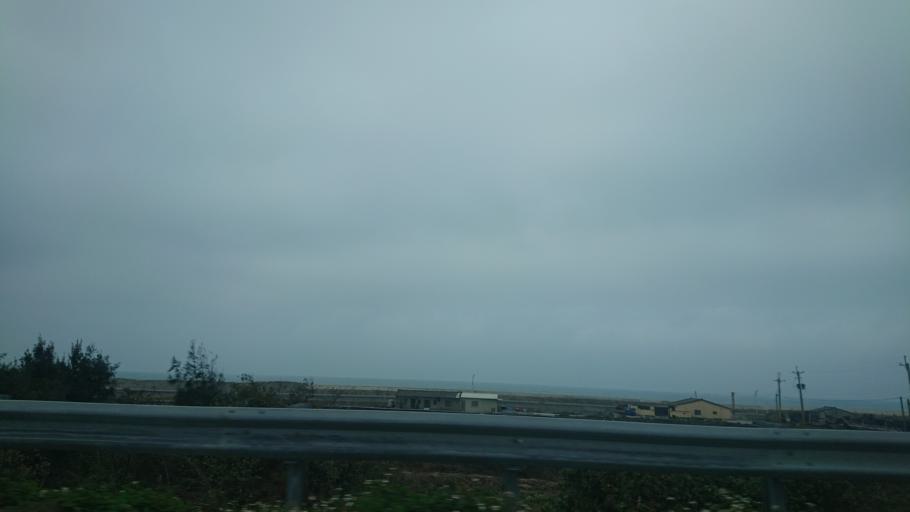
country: TW
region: Taiwan
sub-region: Miaoli
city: Miaoli
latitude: 24.5177
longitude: 120.6865
